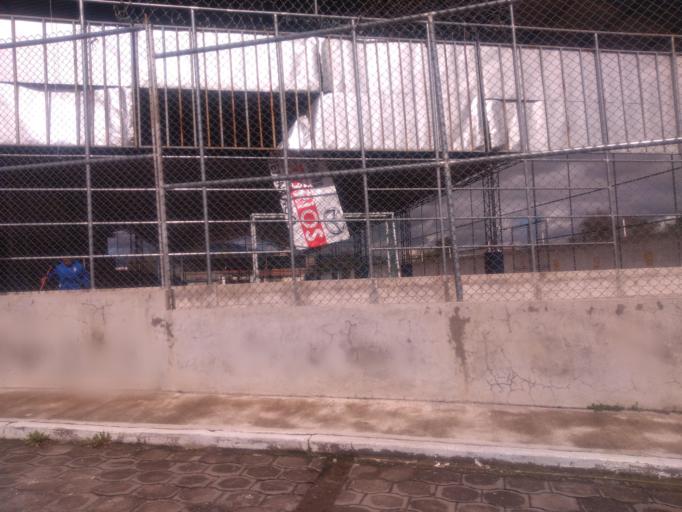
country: GT
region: Quetzaltenango
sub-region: Municipio de La Esperanza
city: La Esperanza
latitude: 14.8686
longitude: -91.5656
